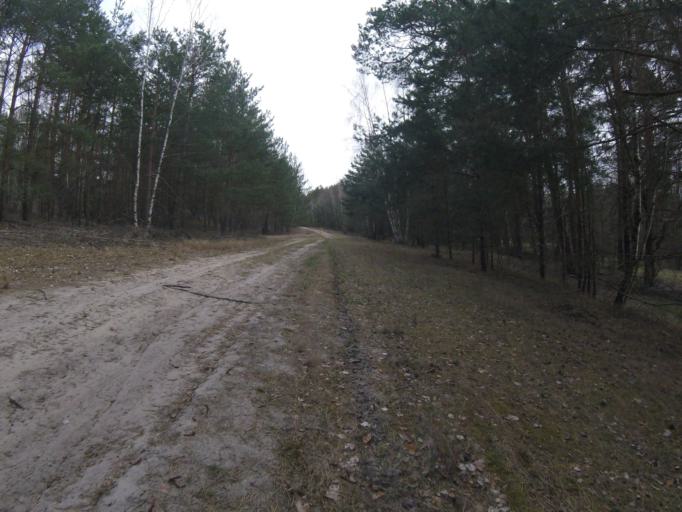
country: DE
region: Brandenburg
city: Schwerin
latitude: 52.1812
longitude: 13.6386
